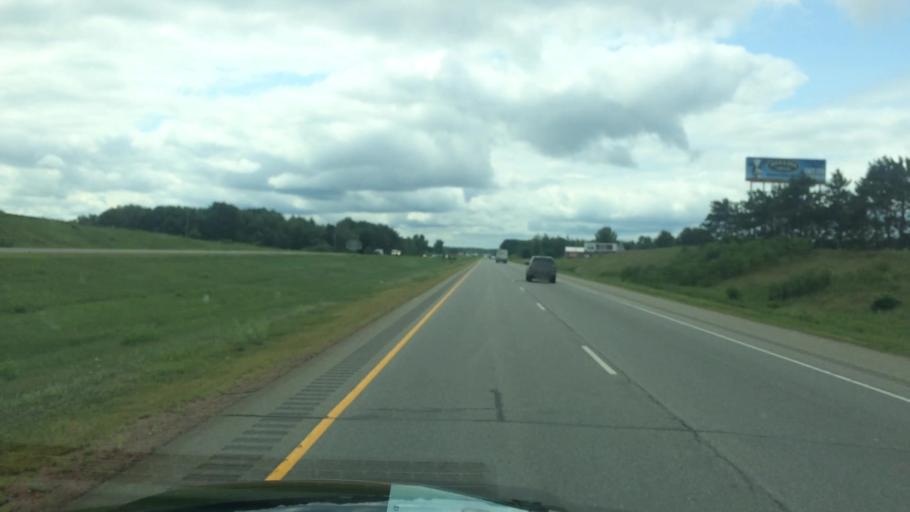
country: US
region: Wisconsin
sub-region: Marathon County
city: Mosinee
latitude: 44.7606
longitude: -89.6803
